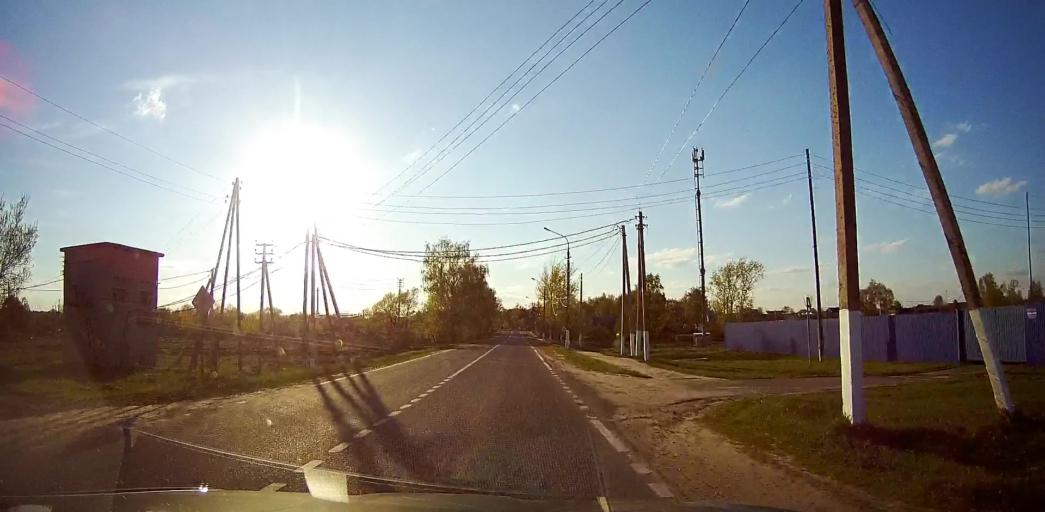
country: RU
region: Moskovskaya
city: Malino
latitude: 55.2778
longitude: 38.1641
